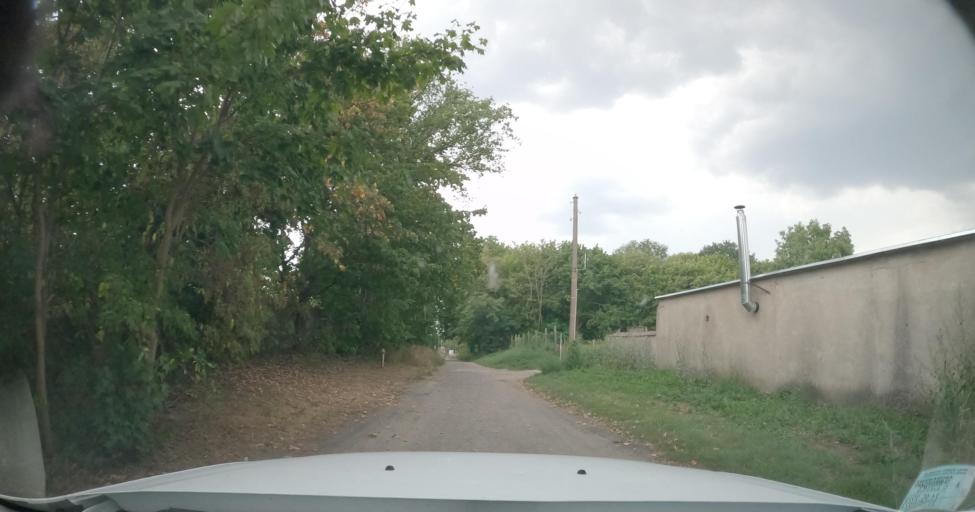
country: PL
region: West Pomeranian Voivodeship
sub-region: Powiat stargardzki
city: Stargard Szczecinski
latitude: 53.3478
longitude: 15.0612
